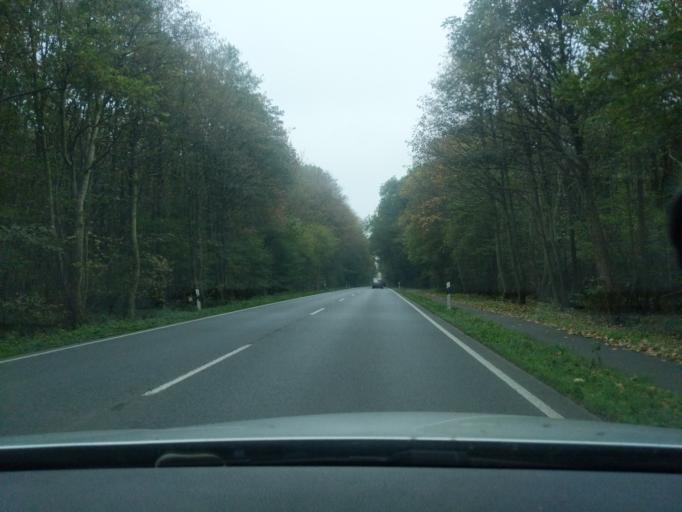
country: DE
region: Lower Saxony
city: Himmelpforten
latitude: 53.6016
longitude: 9.3212
